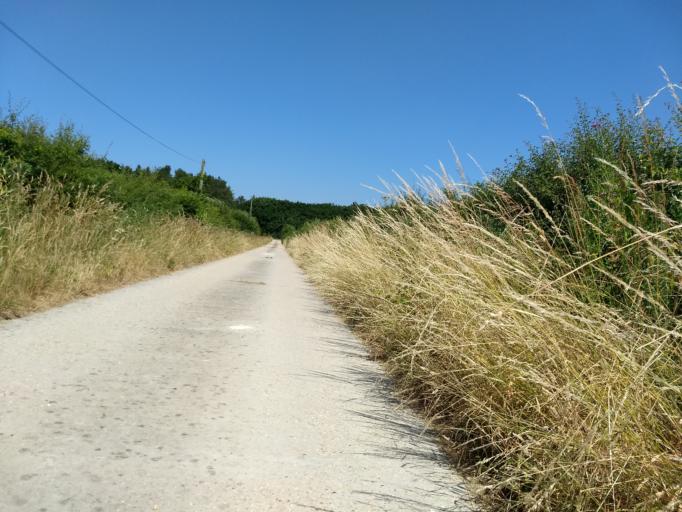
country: GB
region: England
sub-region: Isle of Wight
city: Newport
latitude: 50.7029
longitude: -1.3304
